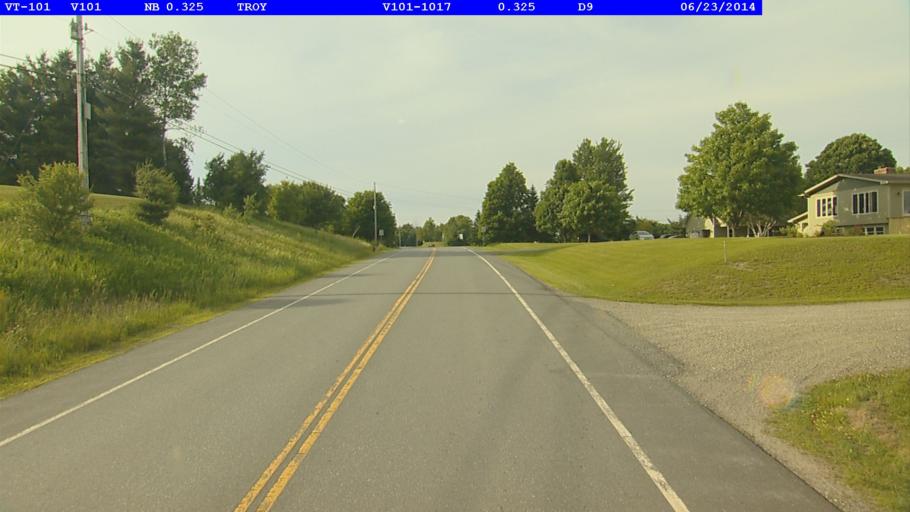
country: US
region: Vermont
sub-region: Orleans County
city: Newport
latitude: 44.9083
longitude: -72.4050
